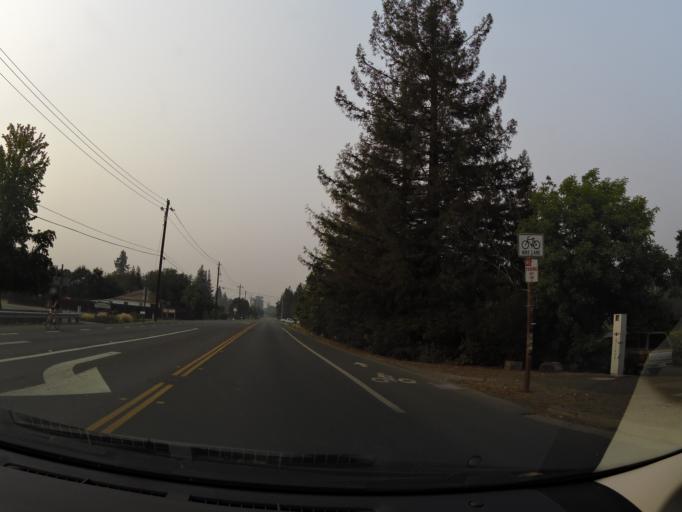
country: US
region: California
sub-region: Sonoma County
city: El Verano
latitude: 38.2999
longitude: -122.4925
